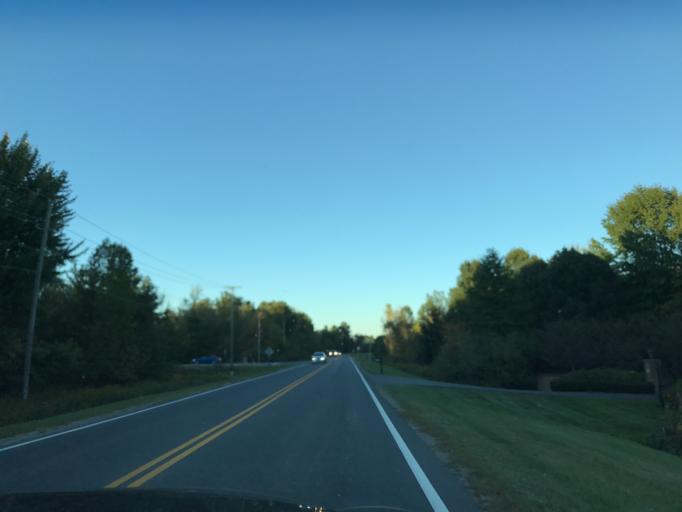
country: US
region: Ohio
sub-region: Franklin County
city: Westerville
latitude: 40.1701
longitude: -82.8802
